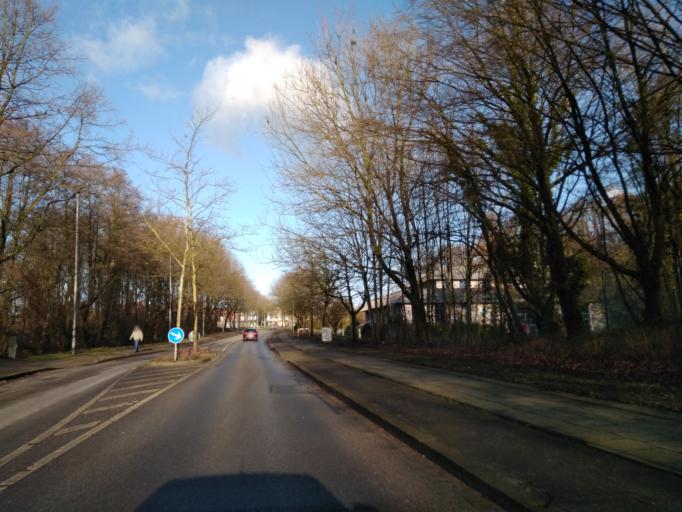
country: DE
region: North Rhine-Westphalia
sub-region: Regierungsbezirk Munster
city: Gladbeck
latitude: 51.5853
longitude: 6.9579
